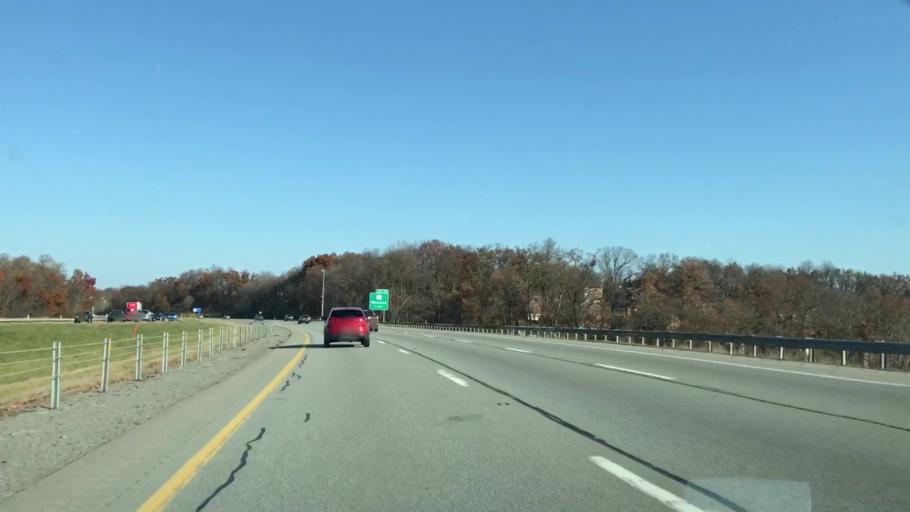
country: US
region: Pennsylvania
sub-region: Allegheny County
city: Franklin Park
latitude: 40.5951
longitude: -80.0945
